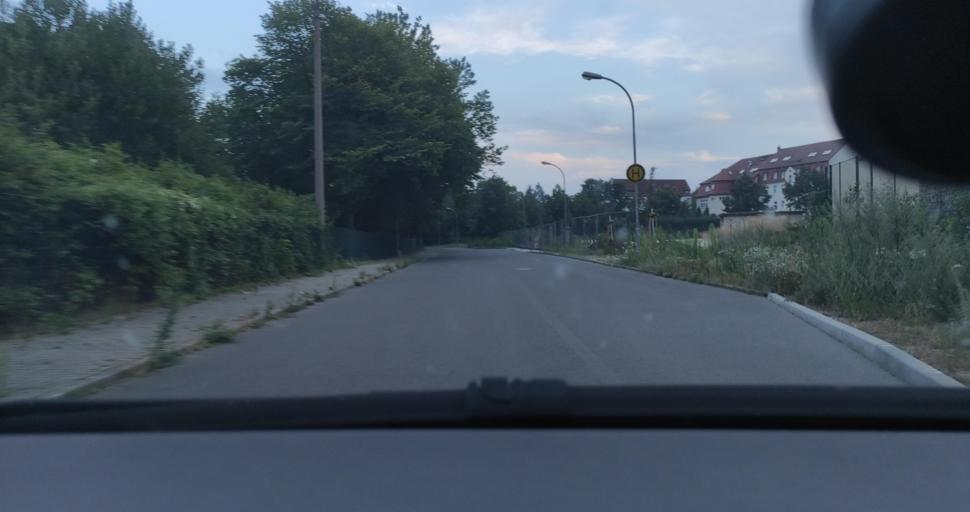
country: DE
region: Brandenburg
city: Forst
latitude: 51.7360
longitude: 14.6426
